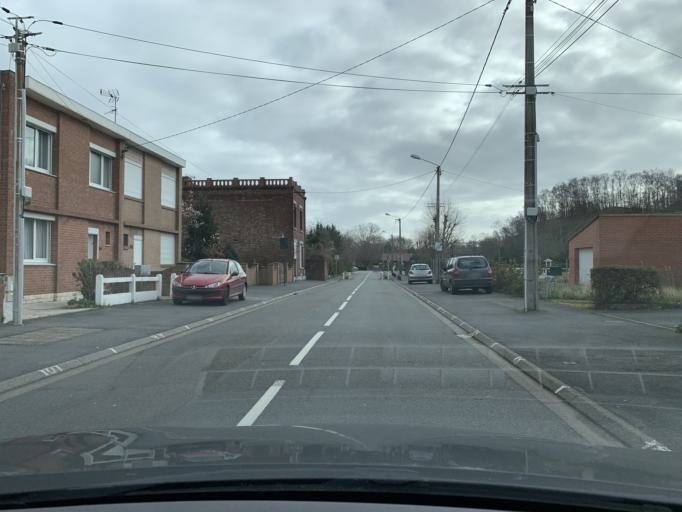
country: FR
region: Nord-Pas-de-Calais
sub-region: Departement du Nord
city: Roost-Warendin
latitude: 50.4068
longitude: 3.1054
